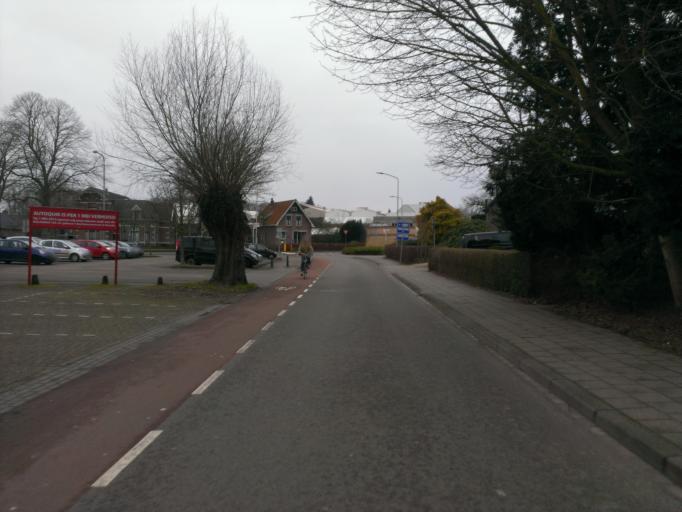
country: NL
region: Gelderland
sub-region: Gemeente Heerde
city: Heerde
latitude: 52.3895
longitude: 6.0403
